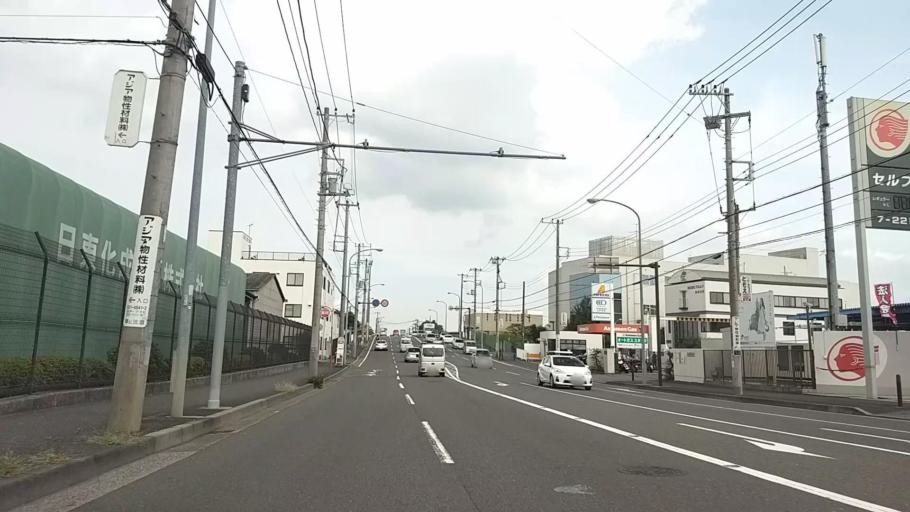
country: JP
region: Tokyo
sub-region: Machida-shi
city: Machida
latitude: 35.5131
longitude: 139.5499
